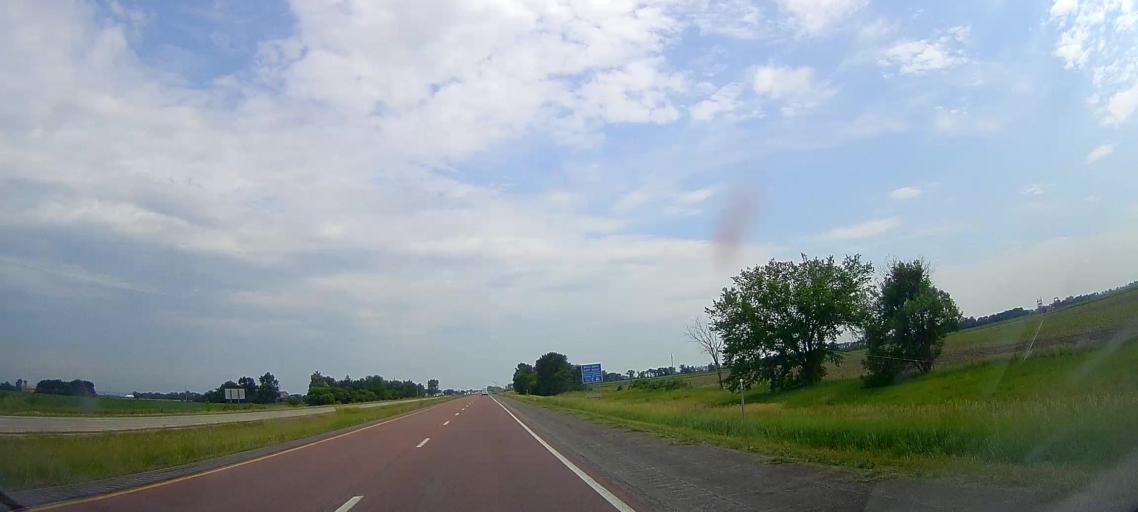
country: US
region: Iowa
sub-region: Monona County
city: Onawa
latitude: 42.0012
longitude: -96.1146
